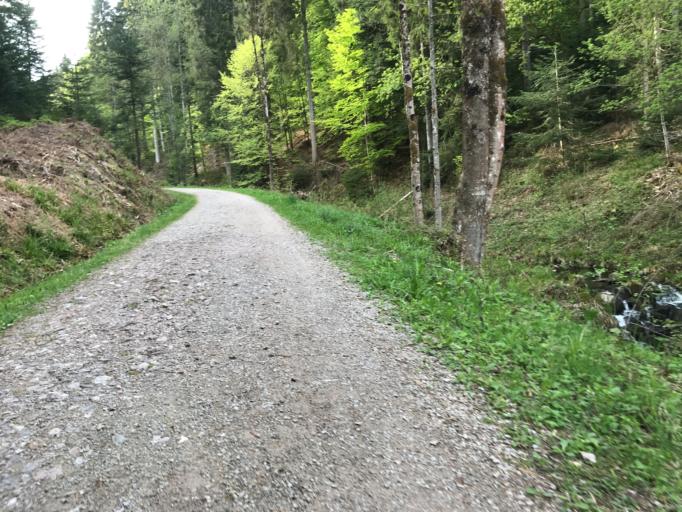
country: DE
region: Baden-Wuerttemberg
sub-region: Karlsruhe Region
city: Baiersbronn
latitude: 48.4830
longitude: 8.3450
